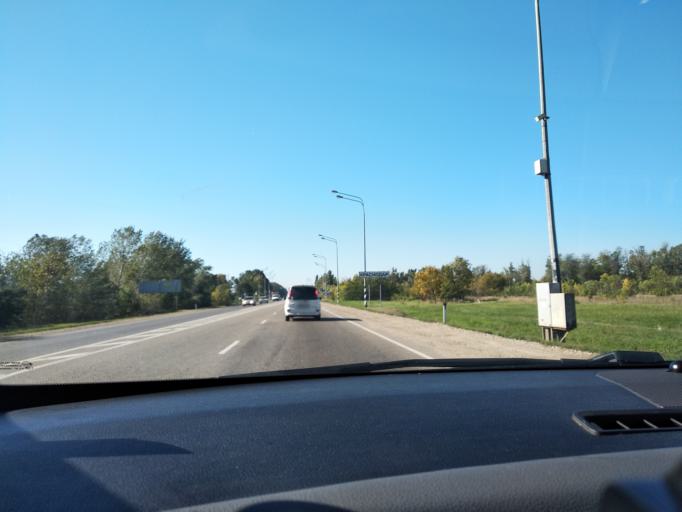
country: RU
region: Krasnodarskiy
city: Novotitarovskaya
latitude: 45.1521
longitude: 39.0624
